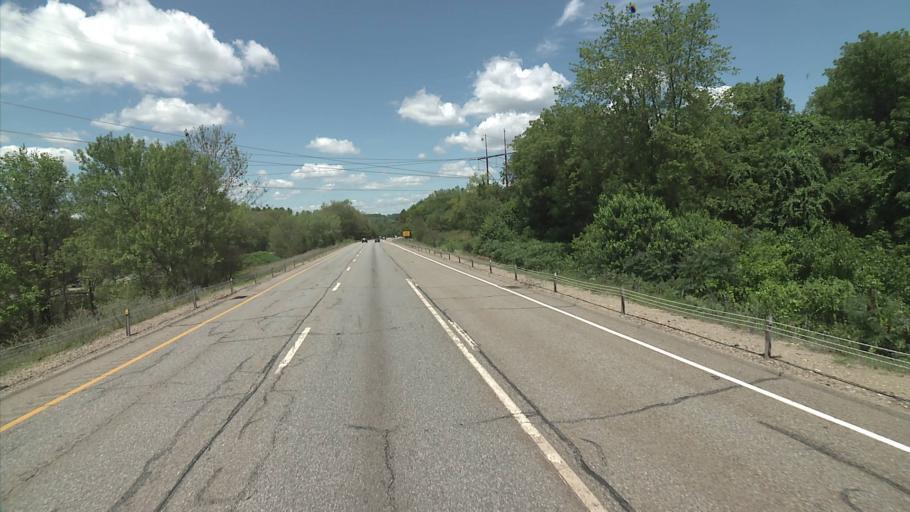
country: US
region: Connecticut
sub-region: Windham County
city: Putnam
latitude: 41.8770
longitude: -71.8942
